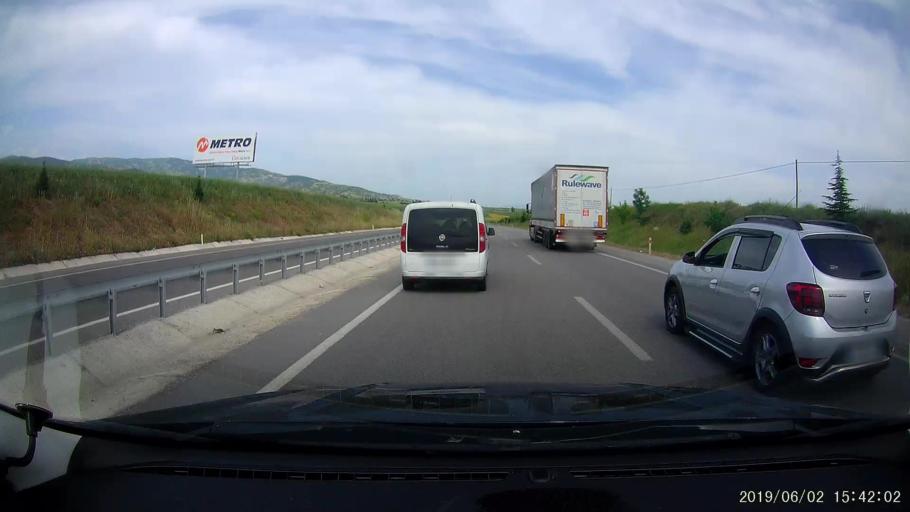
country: TR
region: Amasya
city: Alicik
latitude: 40.8664
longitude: 35.3075
